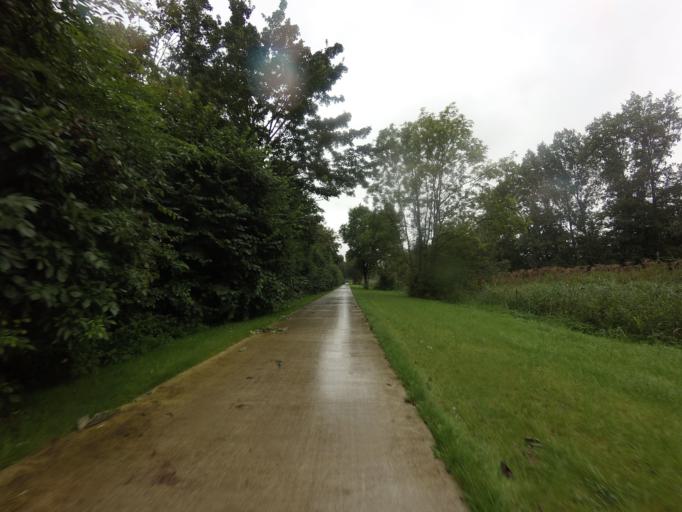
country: NL
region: Flevoland
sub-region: Gemeente Almere
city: Almere Stad
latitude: 52.3452
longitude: 5.1872
